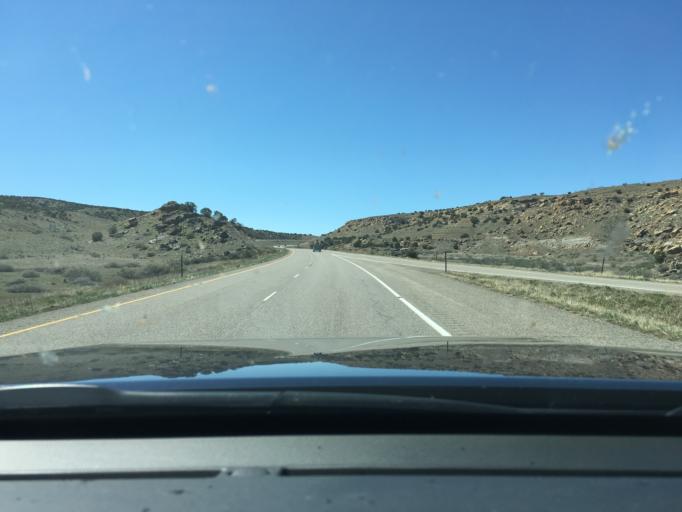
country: US
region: Colorado
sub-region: Mesa County
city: Loma
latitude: 39.1907
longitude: -109.0231
